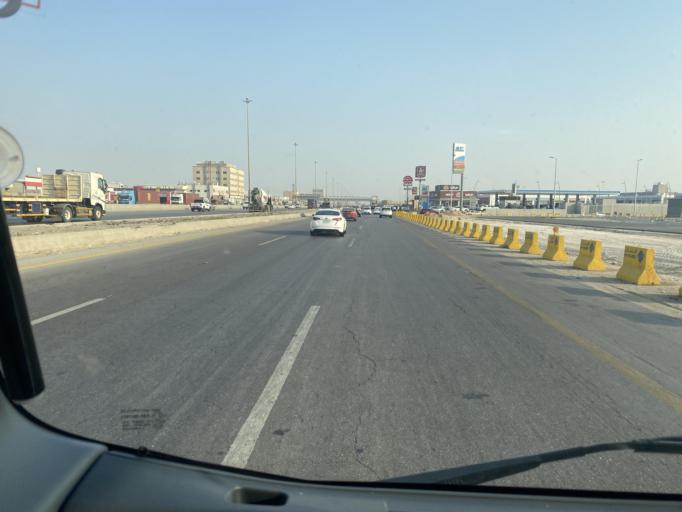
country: SA
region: Eastern Province
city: Sayhat
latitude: 26.4085
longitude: 50.0141
